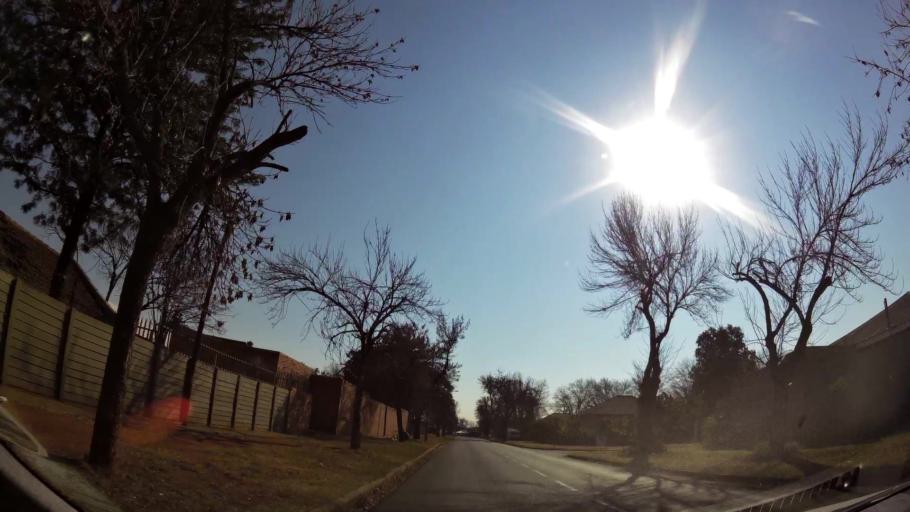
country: ZA
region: Gauteng
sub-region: Ekurhuleni Metropolitan Municipality
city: Boksburg
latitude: -26.2261
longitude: 28.2610
